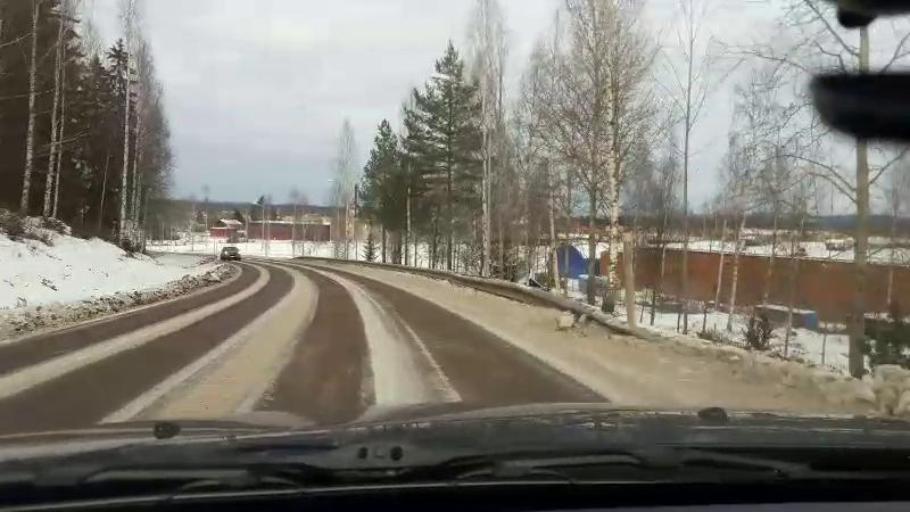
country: SE
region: Gaevleborg
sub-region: Bollnas Kommun
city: Bollnas
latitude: 61.3355
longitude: 16.3929
